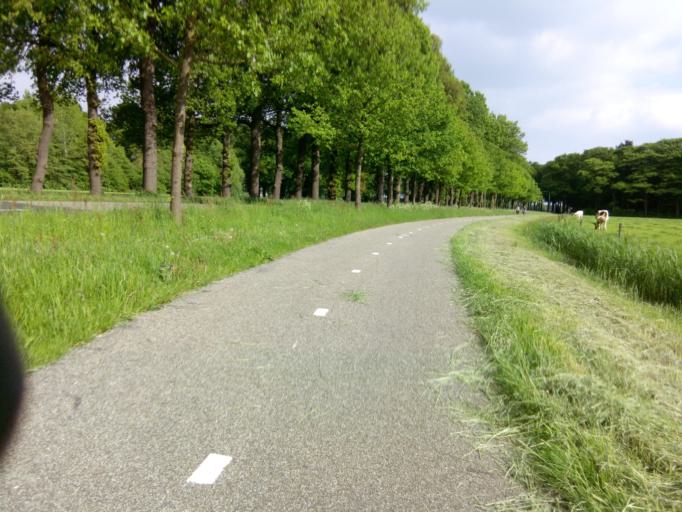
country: NL
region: Gelderland
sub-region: Berkelland
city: Borculo
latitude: 52.0982
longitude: 6.5281
